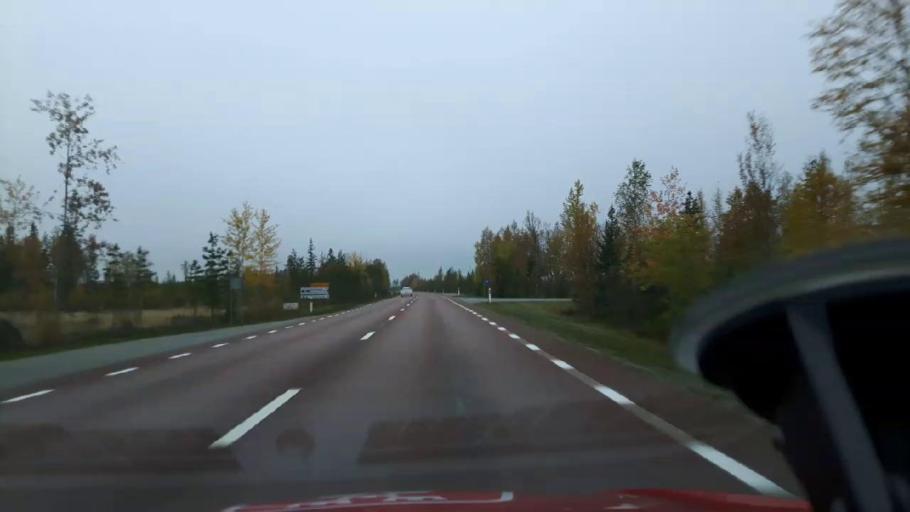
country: SE
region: Jaemtland
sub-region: Bergs Kommun
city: Hoverberg
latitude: 62.5282
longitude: 14.4468
